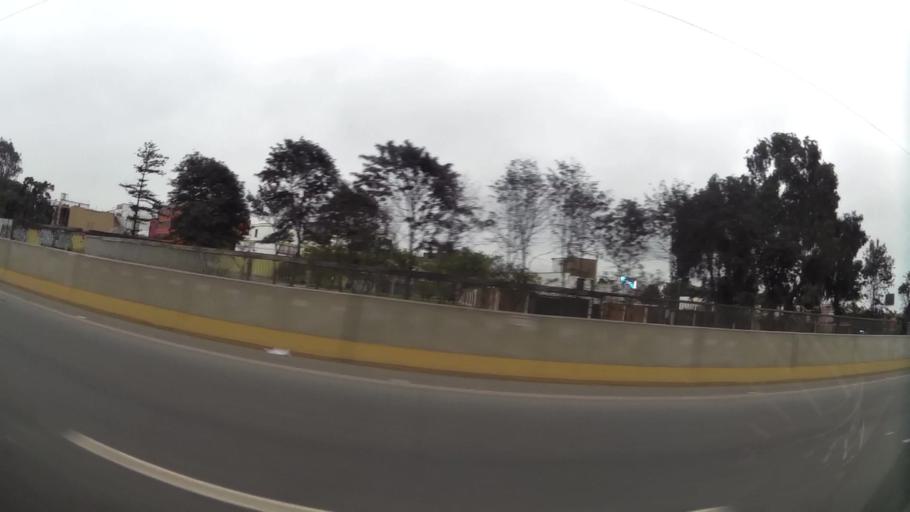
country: PE
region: Lima
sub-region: Lima
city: San Luis
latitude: -12.0824
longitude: -76.9796
